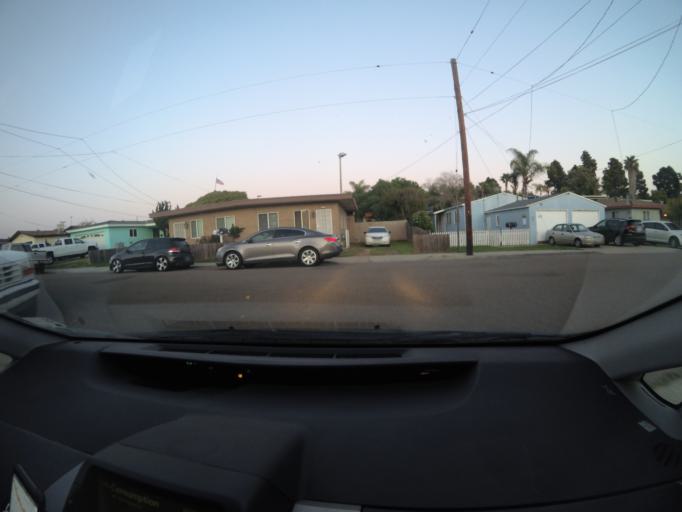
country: US
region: California
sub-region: San Diego County
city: Imperial Beach
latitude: 32.5790
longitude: -117.1167
